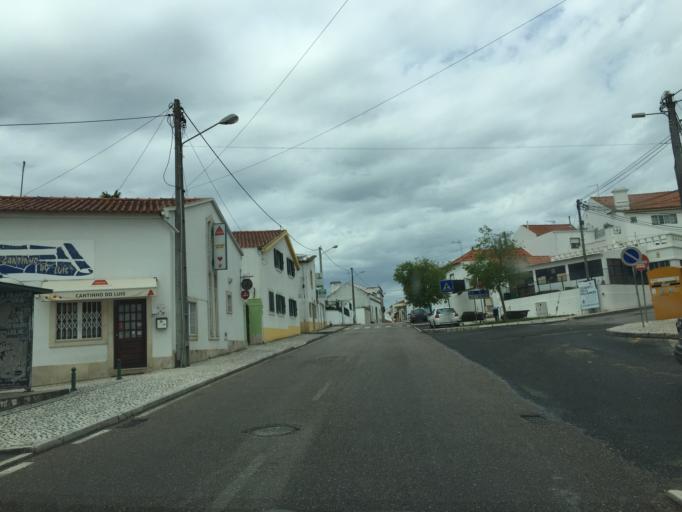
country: PT
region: Lisbon
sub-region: Azambuja
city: Aveiras de Cima
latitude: 39.1350
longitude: -8.8976
